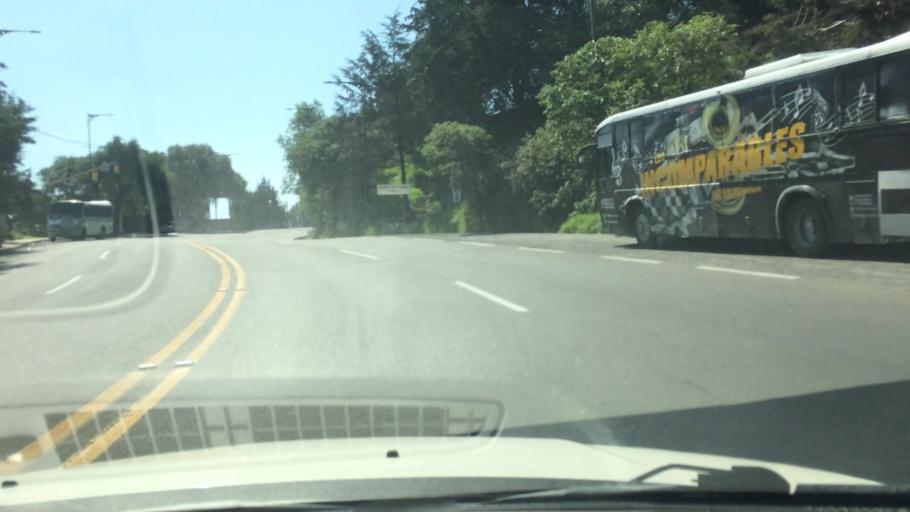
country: MX
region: Mexico City
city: Tlalpan
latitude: 19.2419
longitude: -99.1672
